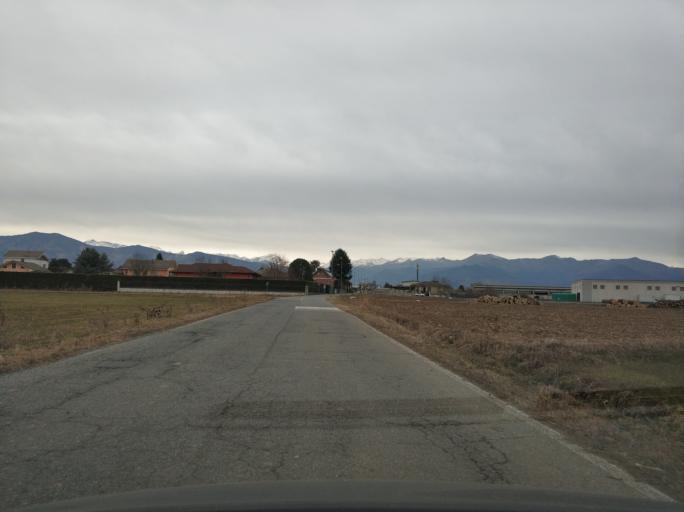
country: IT
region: Piedmont
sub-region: Provincia di Torino
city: San Maurizio
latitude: 45.1928
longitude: 7.6223
